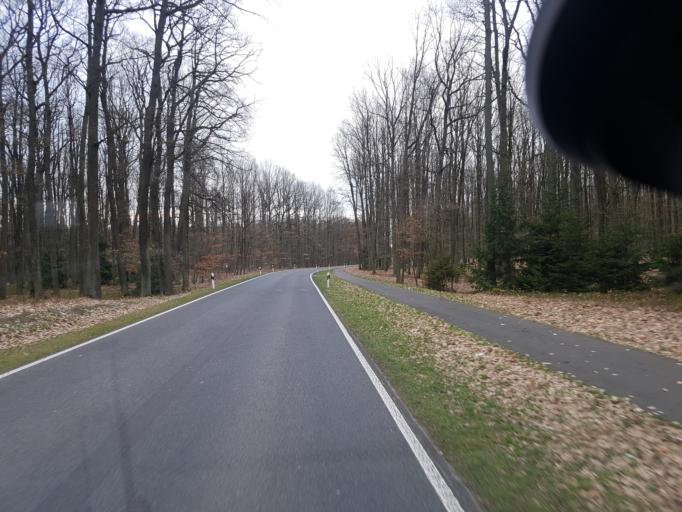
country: DE
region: Brandenburg
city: Gross Lindow
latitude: 52.1705
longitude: 14.4932
